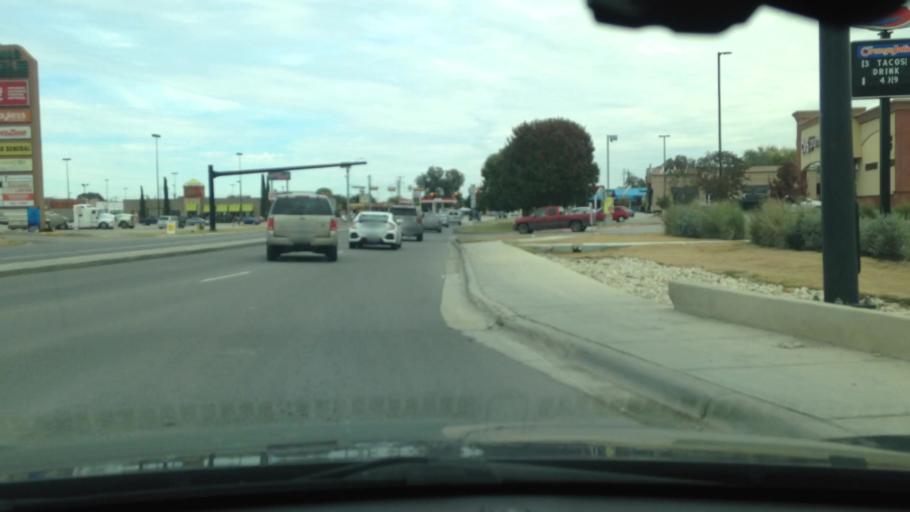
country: US
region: Texas
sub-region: Hays County
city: San Marcos
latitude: 29.8817
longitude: -97.9202
